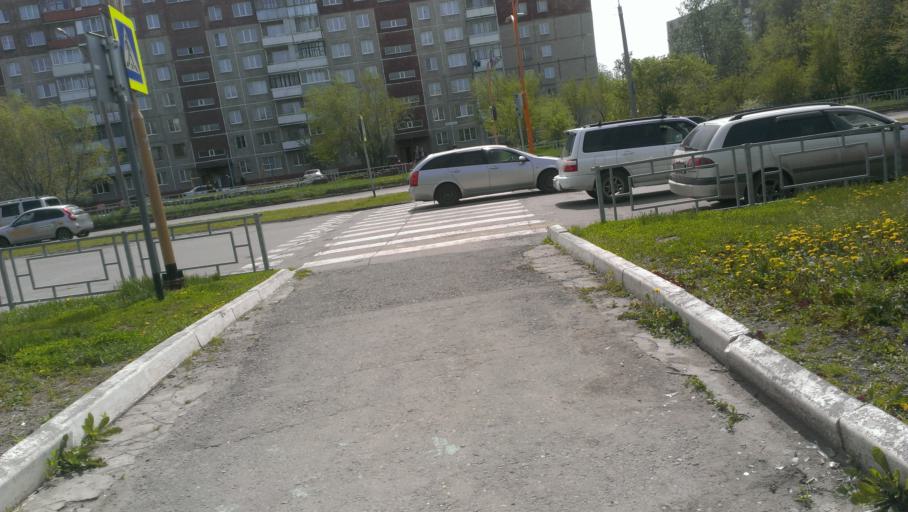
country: RU
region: Altai Krai
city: Novosilikatnyy
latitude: 53.3628
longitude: 83.6684
